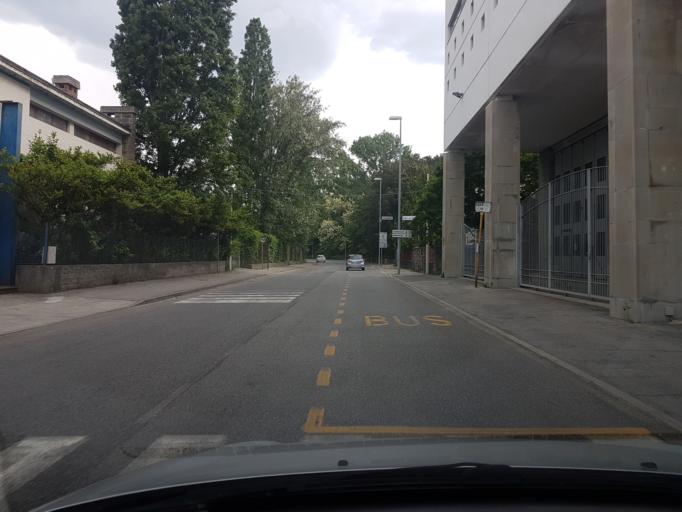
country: IT
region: Friuli Venezia Giulia
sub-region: Provincia di Trieste
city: Muggia
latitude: 45.6003
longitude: 13.7774
